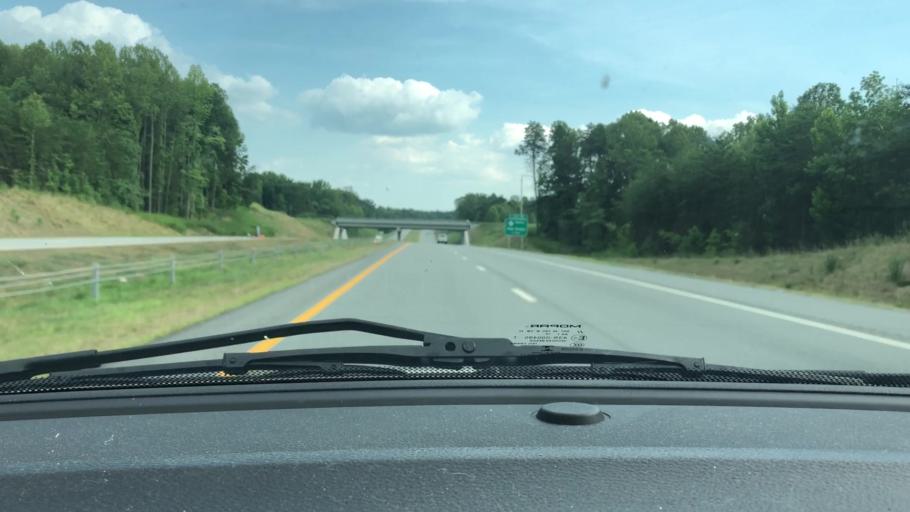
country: US
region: North Carolina
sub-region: Guilford County
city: Oak Ridge
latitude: 36.1552
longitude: -79.9596
